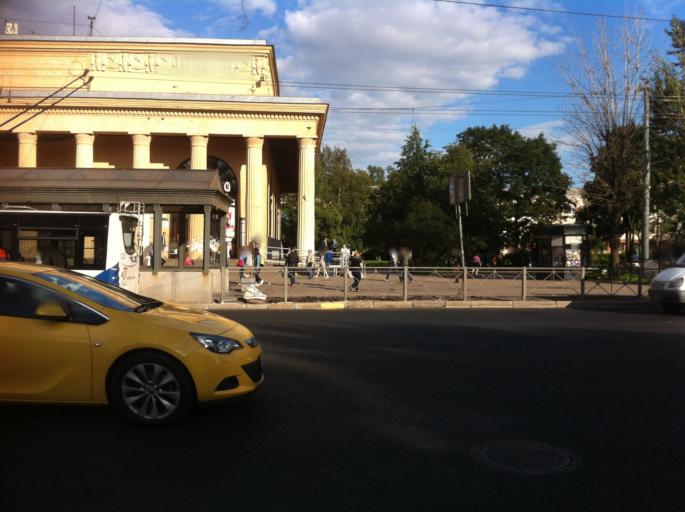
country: RU
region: St.-Petersburg
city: Avtovo
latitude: 59.8798
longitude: 30.2609
